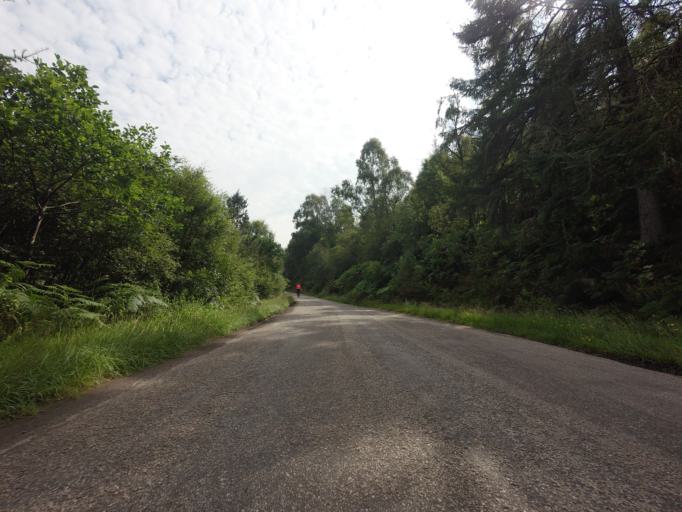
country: GB
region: Scotland
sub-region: Highland
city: Evanton
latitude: 57.9533
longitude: -4.4077
